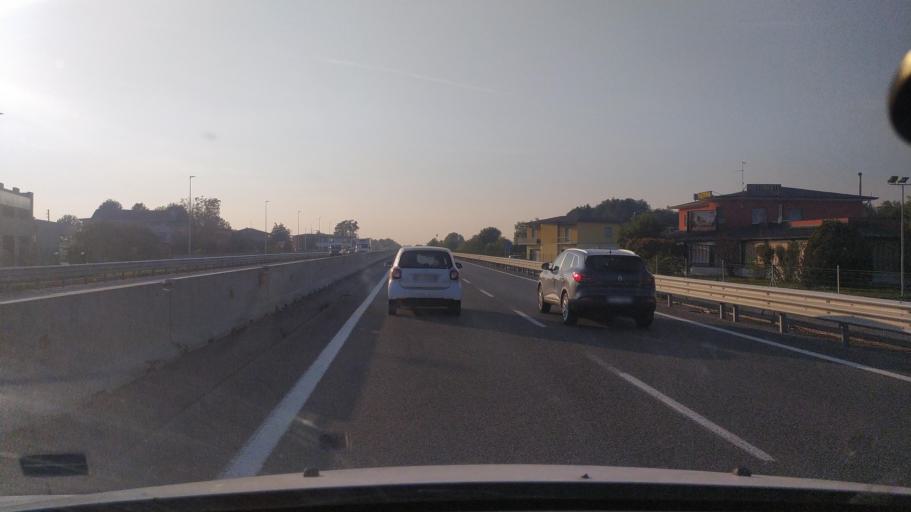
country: IT
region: Lombardy
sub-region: Provincia di Cremona
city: Palazzo Pignano
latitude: 45.3817
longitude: 9.5743
